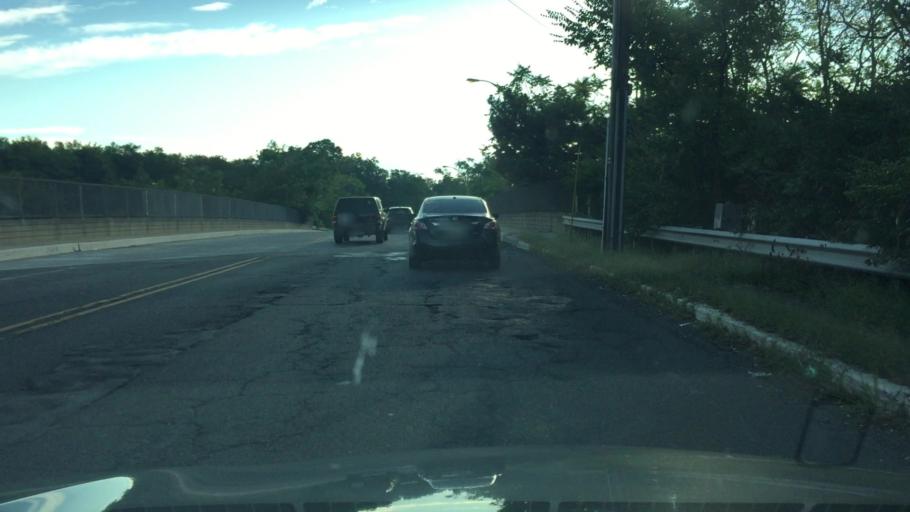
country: US
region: New Jersey
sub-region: Middlesex County
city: Metuchen
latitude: 40.5413
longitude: -74.3904
